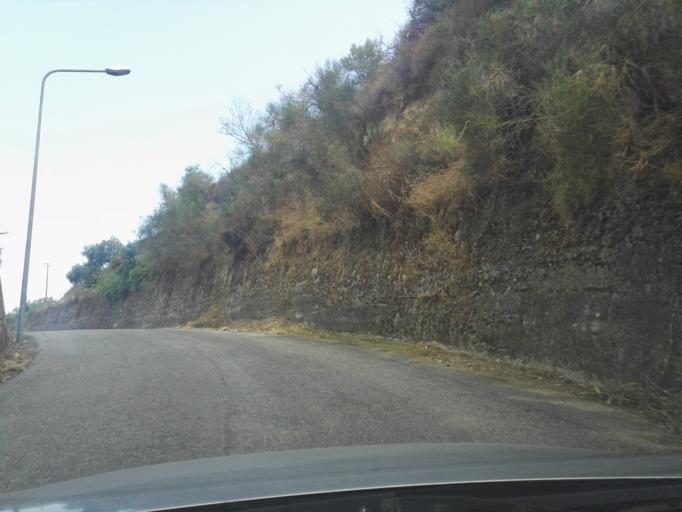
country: IT
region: Calabria
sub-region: Provincia di Reggio Calabria
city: Riace
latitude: 38.4156
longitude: 16.4816
